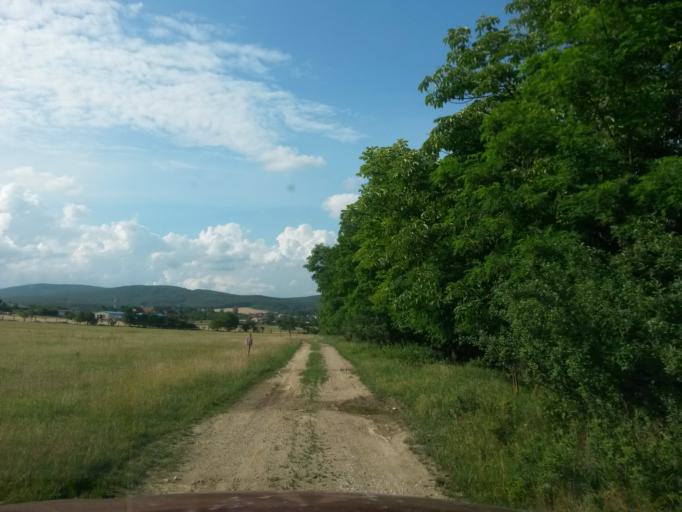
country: SK
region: Kosicky
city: Moldava nad Bodvou
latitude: 48.6661
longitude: 21.1123
